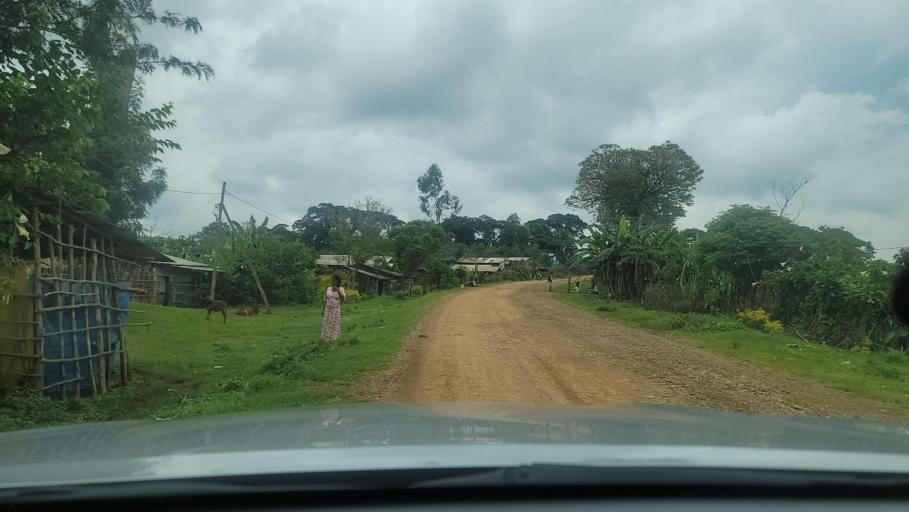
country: ET
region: Oromiya
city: Agaro
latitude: 7.7930
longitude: 36.4428
